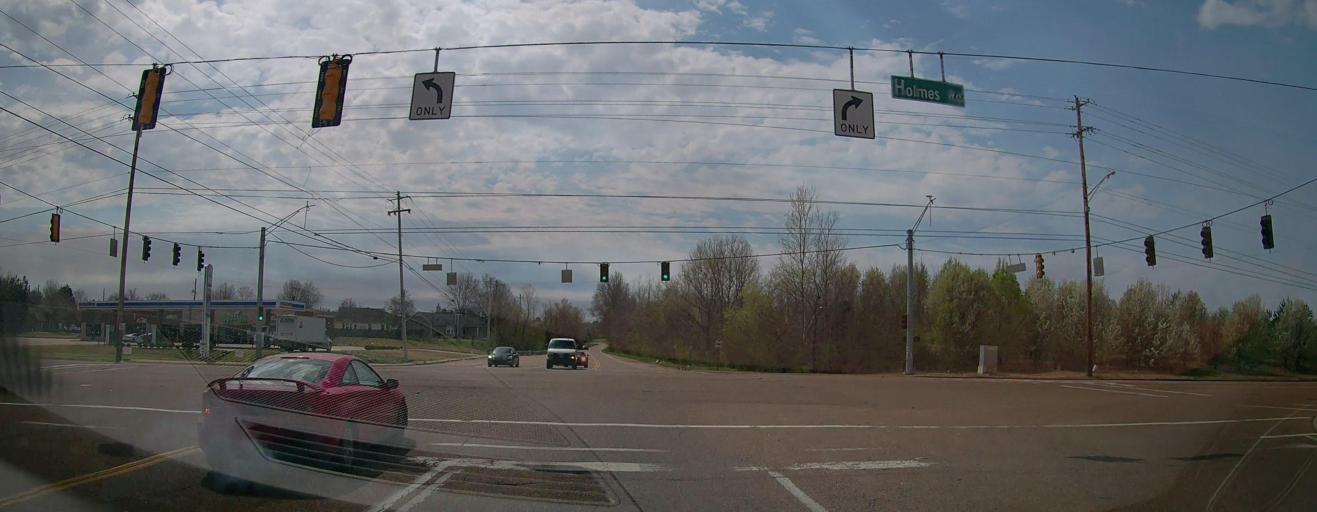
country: US
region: Mississippi
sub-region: De Soto County
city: Olive Branch
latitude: 35.0061
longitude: -89.8486
